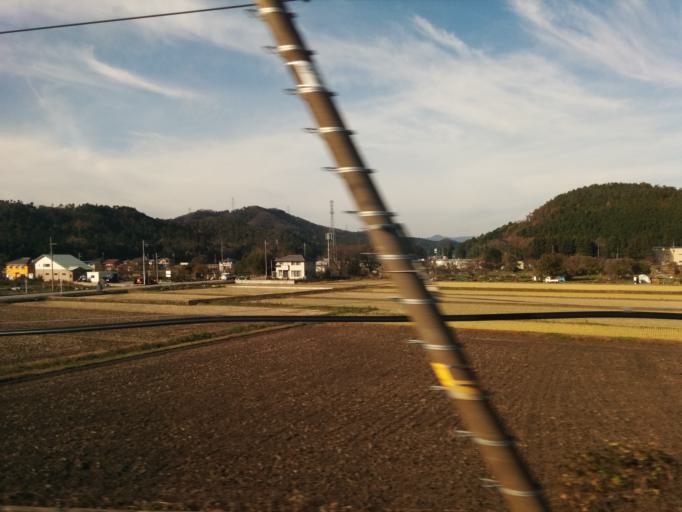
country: JP
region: Shiga Prefecture
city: Nagahama
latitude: 35.3641
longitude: 136.3509
